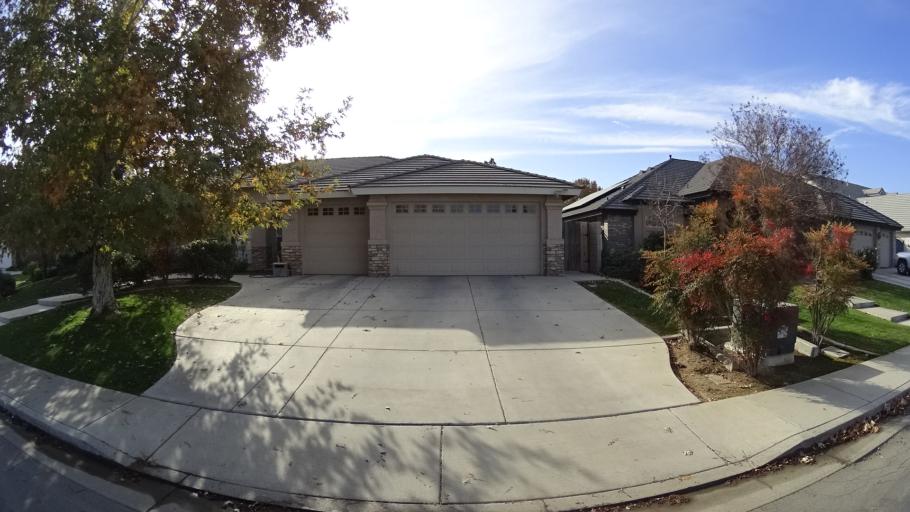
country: US
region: California
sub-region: Kern County
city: Rosedale
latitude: 35.4118
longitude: -119.1334
